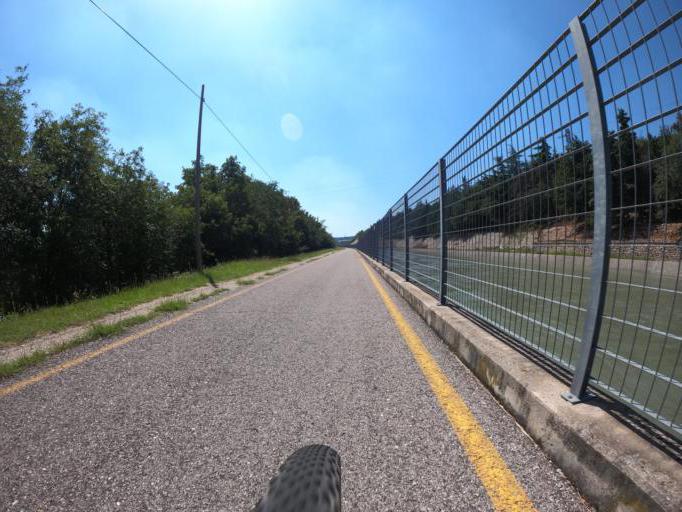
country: IT
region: Veneto
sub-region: Provincia di Verona
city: Volargne
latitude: 45.5427
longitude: 10.8118
